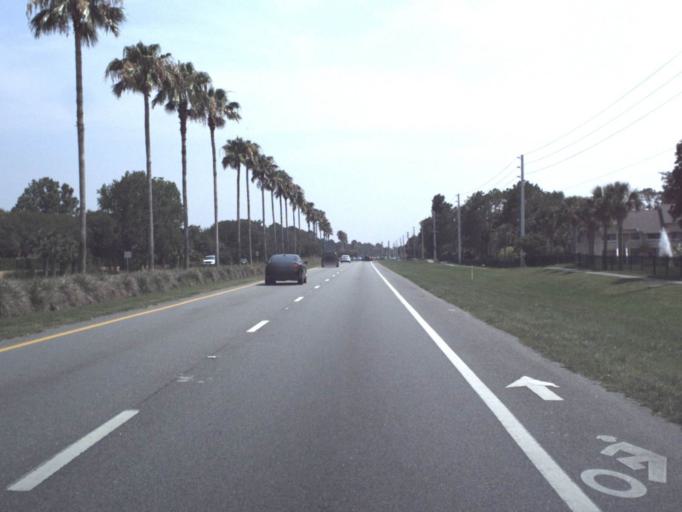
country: US
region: Florida
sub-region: Saint Johns County
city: Sawgrass
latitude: 30.2112
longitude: -81.3807
